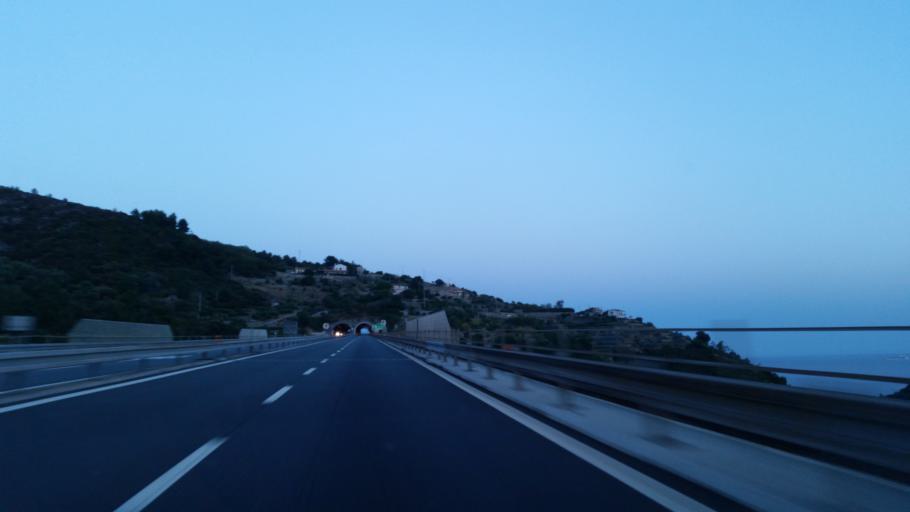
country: IT
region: Liguria
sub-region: Provincia di Imperia
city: Vallebona
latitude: 43.7985
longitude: 7.6711
